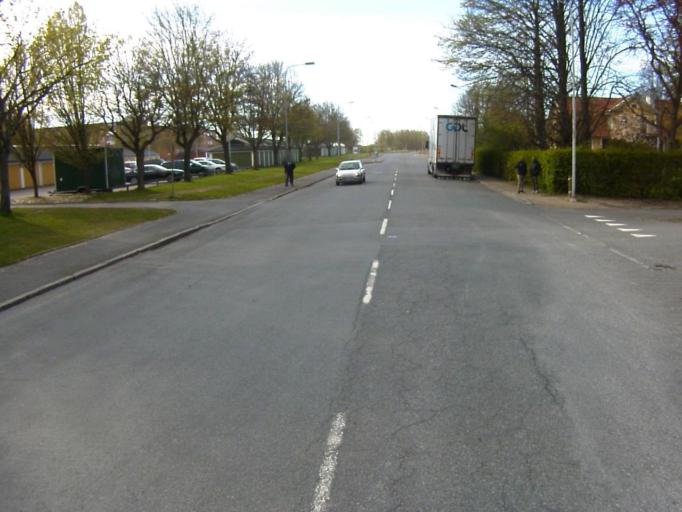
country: SE
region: Skane
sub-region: Kristianstads Kommun
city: Kristianstad
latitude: 56.0614
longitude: 14.1600
